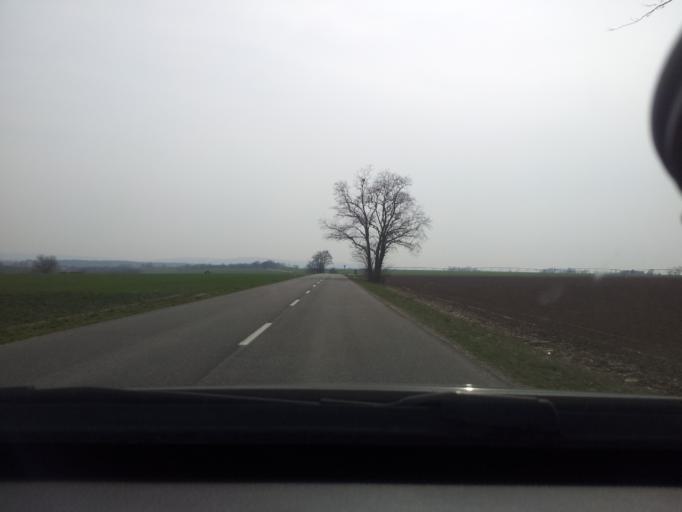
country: SK
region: Trnavsky
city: Leopoldov
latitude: 48.4678
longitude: 17.6968
